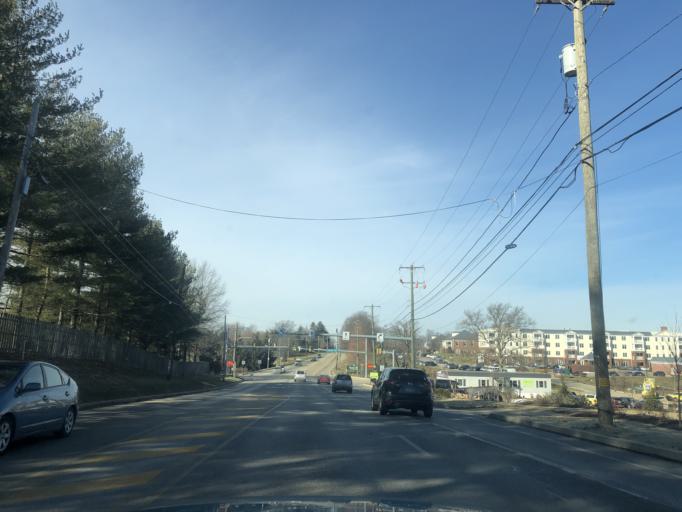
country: US
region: Pennsylvania
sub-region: Montgomery County
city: Plymouth Meeting
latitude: 40.0756
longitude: -75.2460
